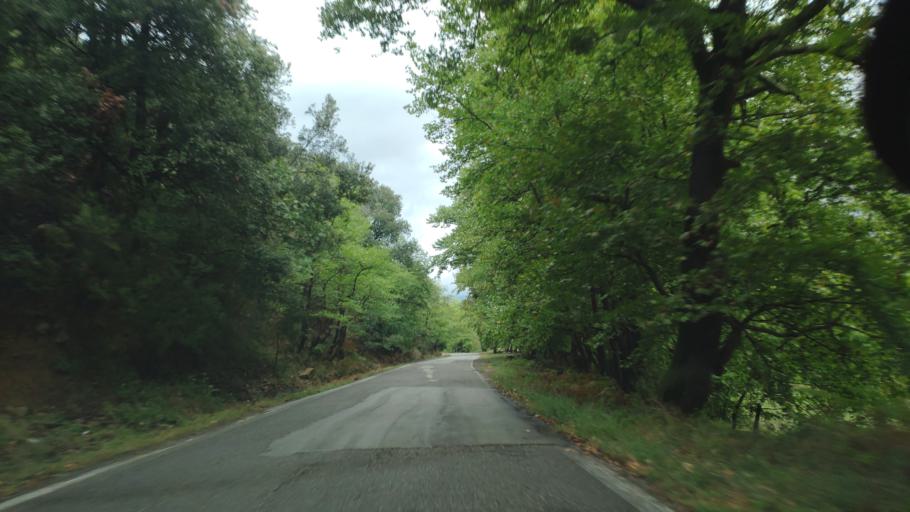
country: GR
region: West Greece
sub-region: Nomos Aitolias kai Akarnanias
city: Krikellos
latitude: 38.9555
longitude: 21.3386
